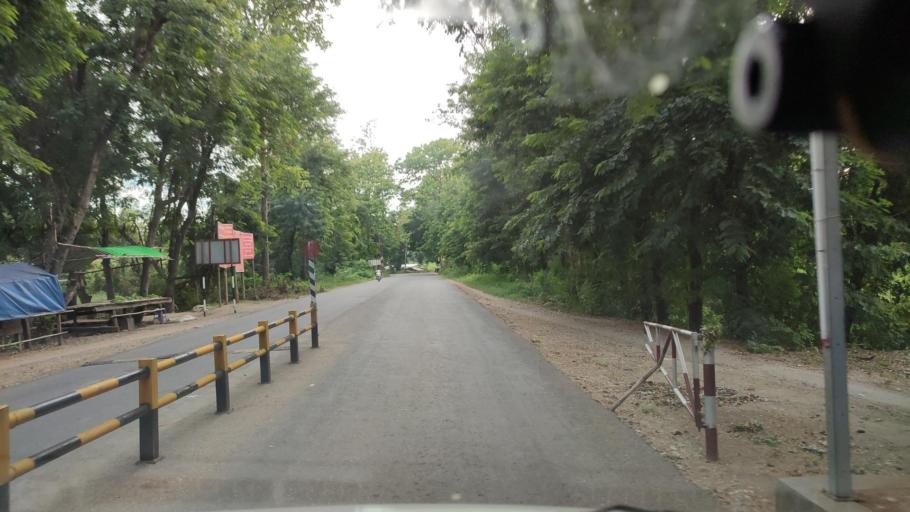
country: MM
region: Magway
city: Yenangyaung
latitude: 20.3838
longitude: 94.6814
